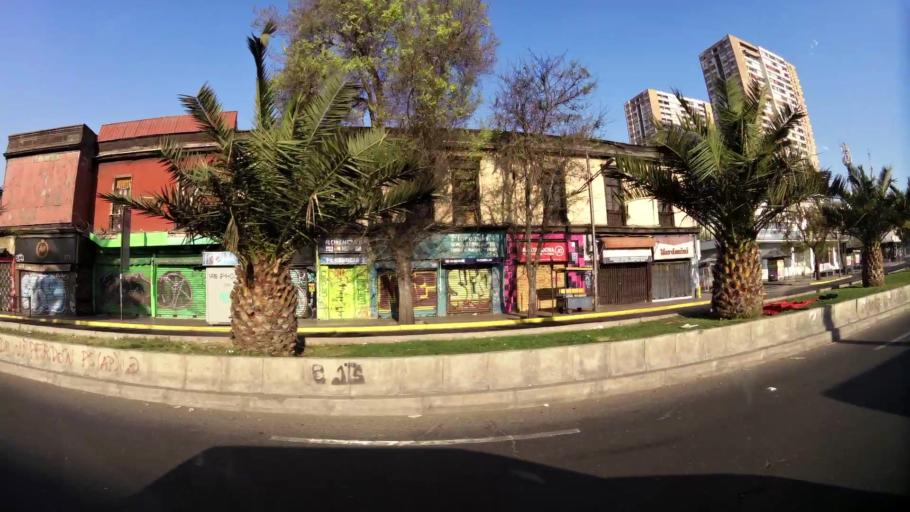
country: CL
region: Santiago Metropolitan
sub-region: Provincia de Santiago
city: Santiago
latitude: -33.4315
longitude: -70.6477
